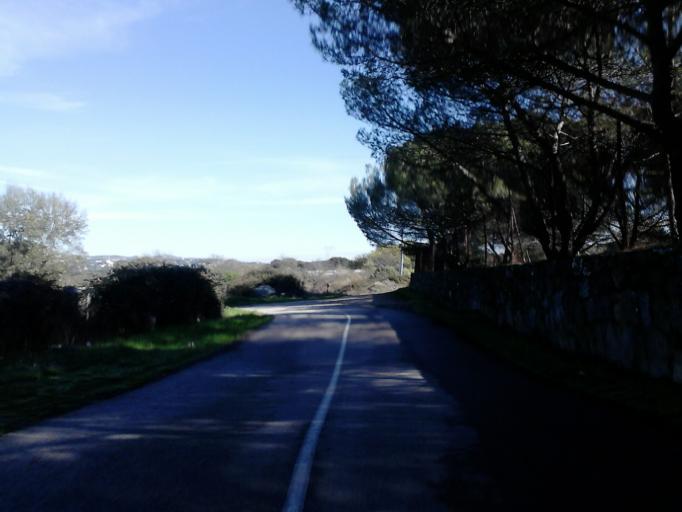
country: ES
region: Madrid
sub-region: Provincia de Madrid
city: Galapagar
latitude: 40.5746
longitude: -3.9908
